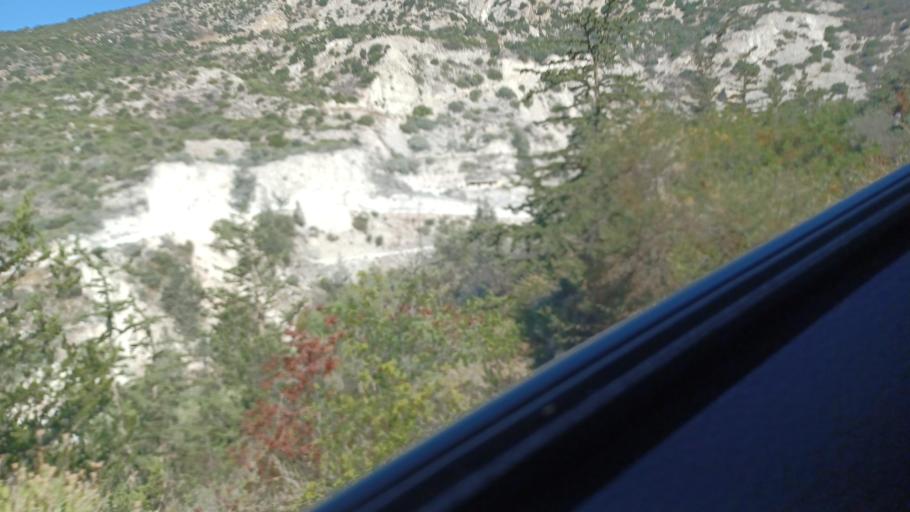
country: CY
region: Pafos
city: Tala
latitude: 34.8687
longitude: 32.4356
